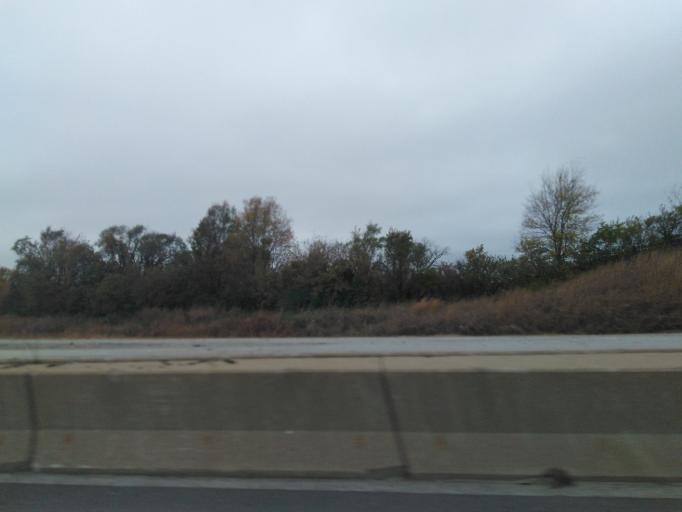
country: US
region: Illinois
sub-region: Saint Clair County
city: Washington Park
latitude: 38.6223
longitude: -90.0678
